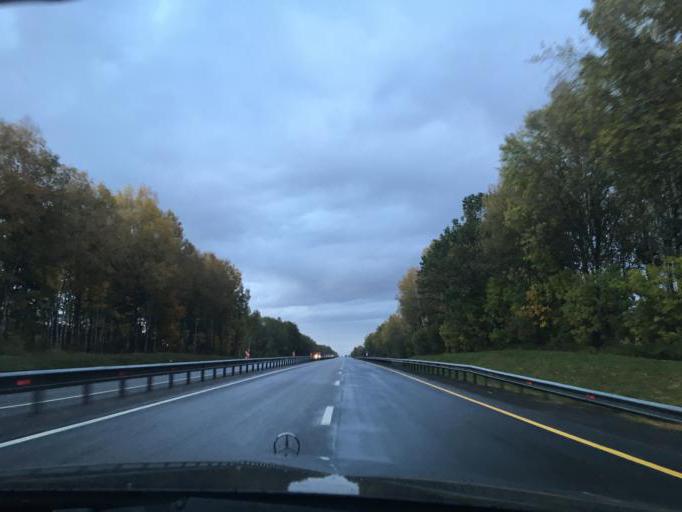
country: RU
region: Smolensk
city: Safonovo
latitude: 55.1242
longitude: 33.1114
